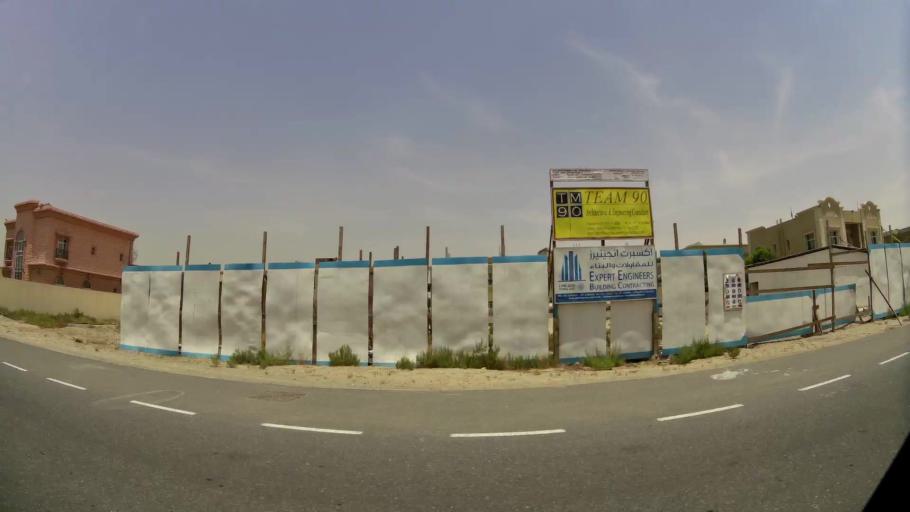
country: AE
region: Ash Shariqah
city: Sharjah
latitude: 25.1994
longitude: 55.3838
